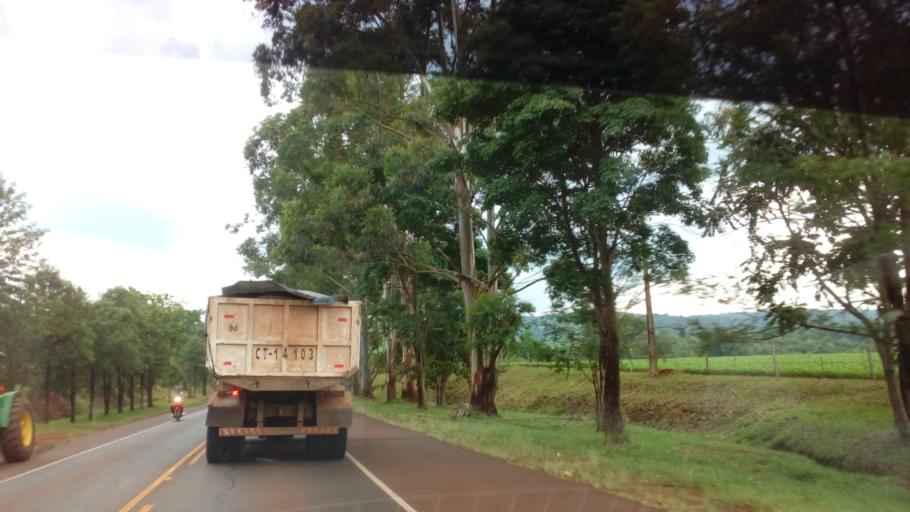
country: PY
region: Itapua
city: Obligado
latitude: -27.0690
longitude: -55.6106
